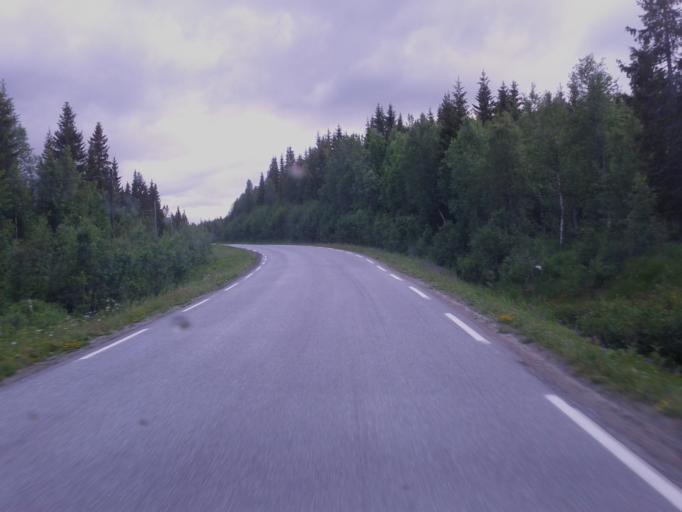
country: NO
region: Nordland
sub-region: Hattfjelldal
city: Hattfjelldal
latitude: 65.5975
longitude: 13.9239
